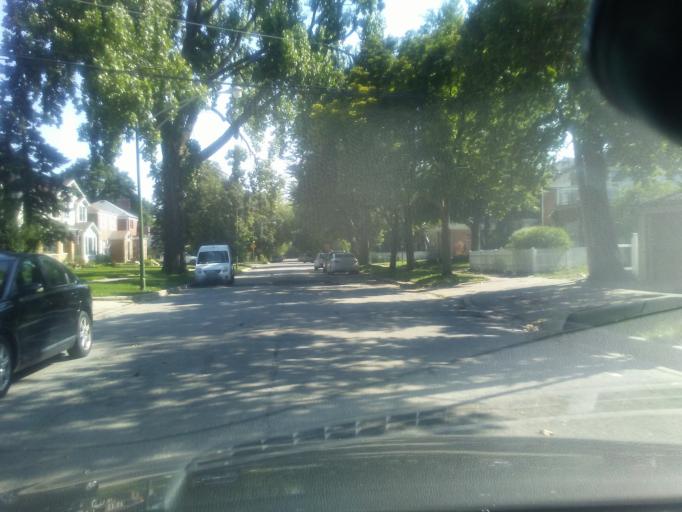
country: US
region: Illinois
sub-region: Cook County
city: Lincolnwood
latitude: 41.9854
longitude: -87.7397
